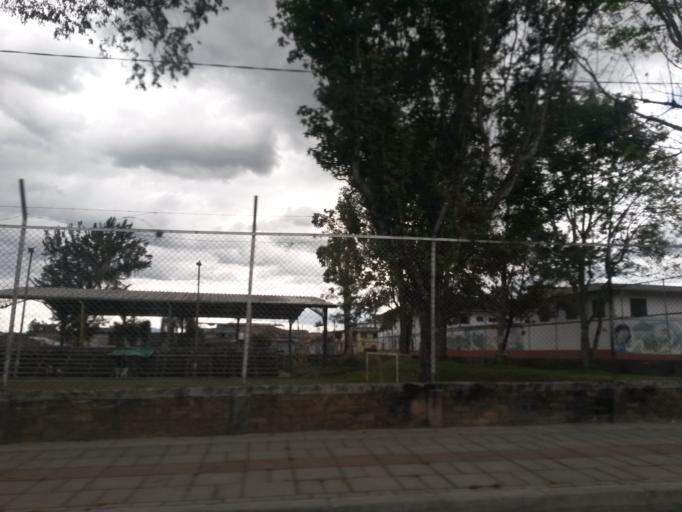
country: CO
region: Cauca
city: Popayan
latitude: 2.4344
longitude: -76.6056
